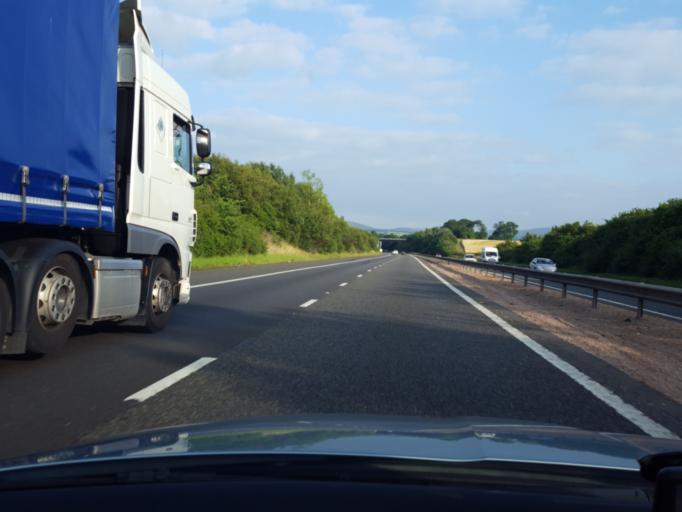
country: GB
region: Scotland
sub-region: Edinburgh
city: Ratho
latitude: 55.9261
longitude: -3.3483
